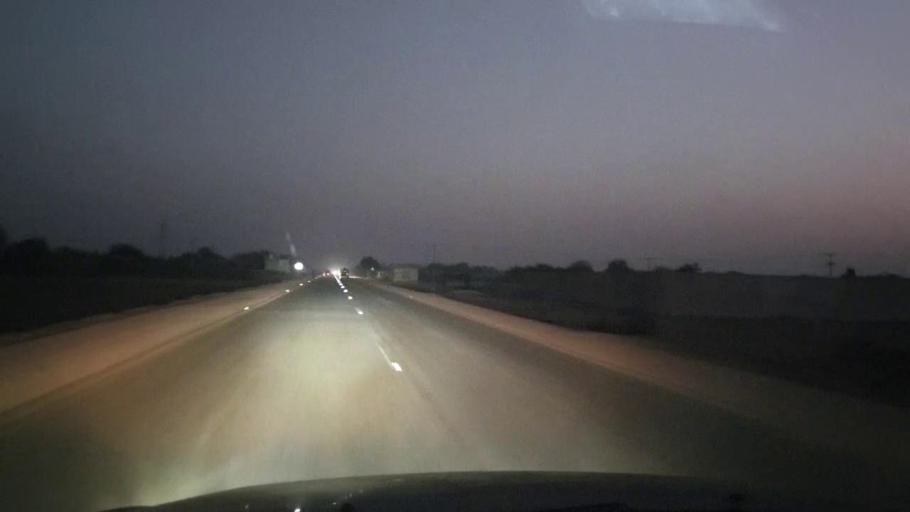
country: PK
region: Sindh
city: Chambar
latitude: 25.3536
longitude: 68.7889
